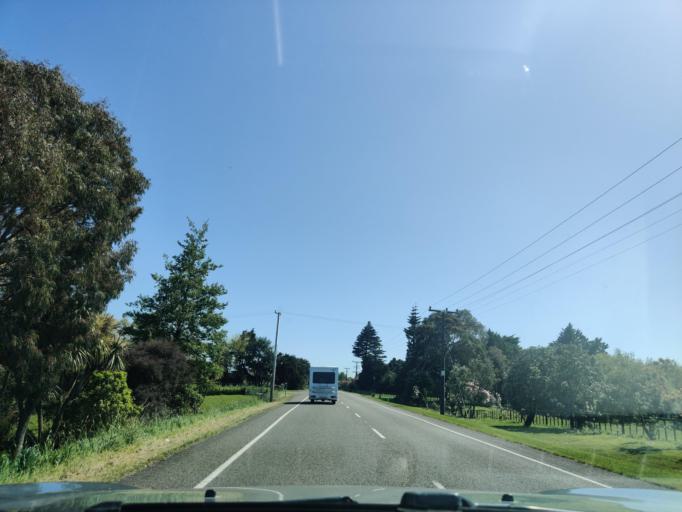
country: NZ
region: Manawatu-Wanganui
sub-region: Wanganui District
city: Wanganui
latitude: -39.8873
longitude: 175.0056
